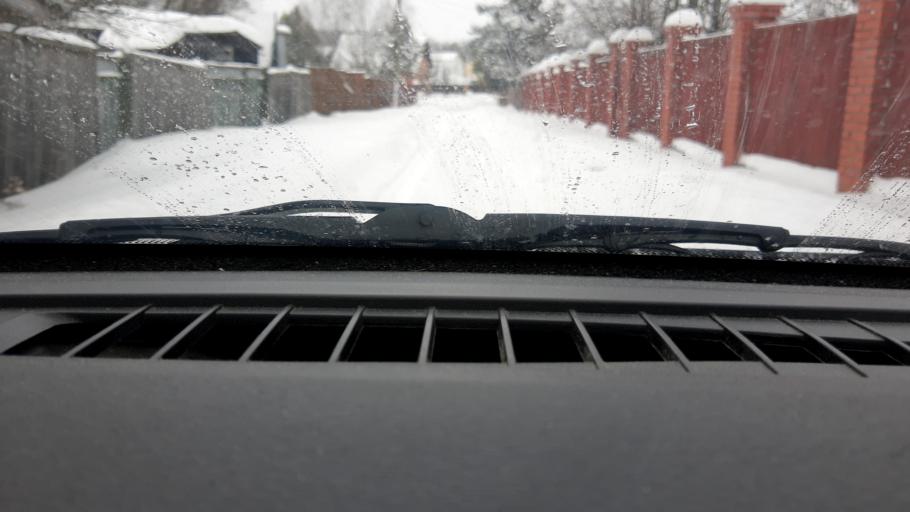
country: RU
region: Moskovskaya
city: Pirogovskiy
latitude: 56.0164
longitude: 37.7261
